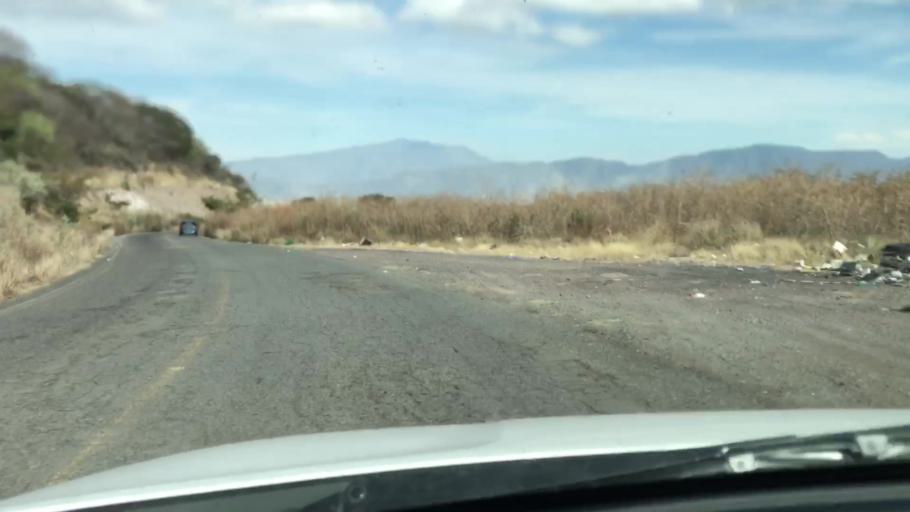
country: MX
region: Jalisco
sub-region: Zacoalco de Torres
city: Barranca de Otates (Barranca de Otatan)
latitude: 20.2445
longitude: -103.6688
